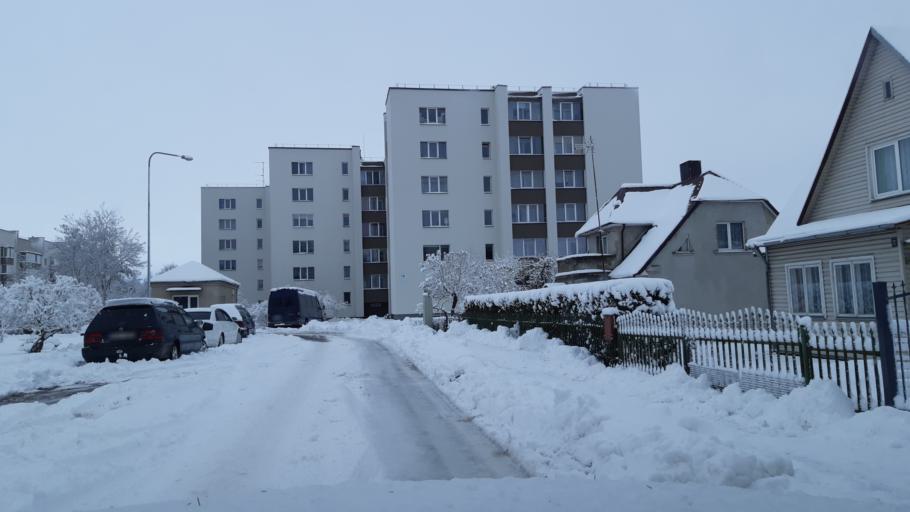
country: LT
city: Kybartai
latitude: 54.6374
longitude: 22.7563
